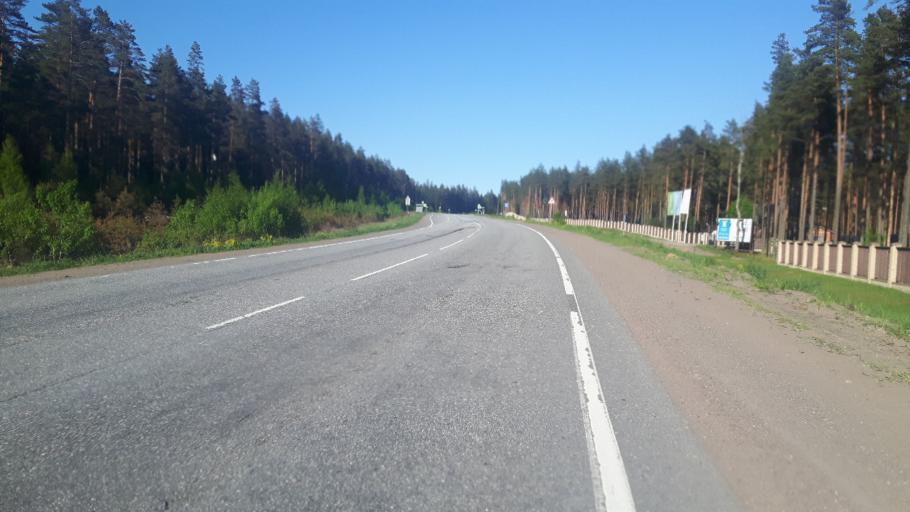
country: RU
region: Leningrad
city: Molodezhnoye
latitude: 60.1706
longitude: 29.2798
